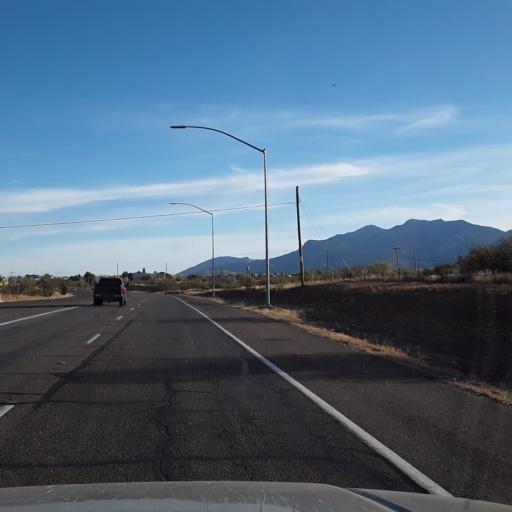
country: US
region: Arizona
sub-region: Cochise County
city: Sierra Vista
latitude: 31.5662
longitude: -110.3119
